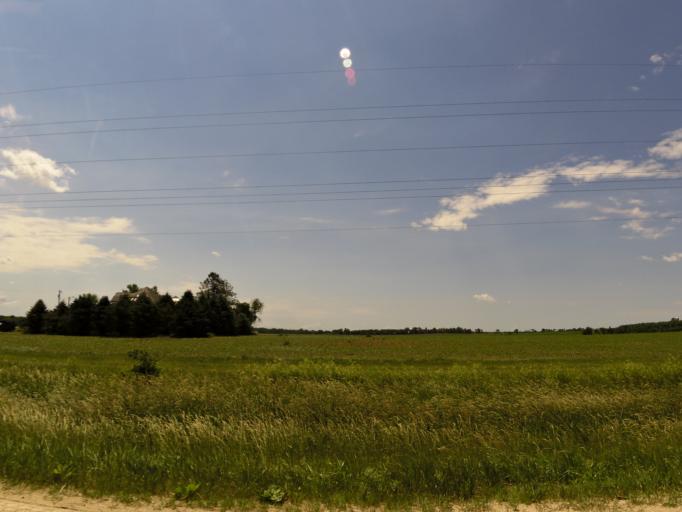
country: US
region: Iowa
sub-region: Bremer County
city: Tripoli
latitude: 42.7148
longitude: -92.1855
